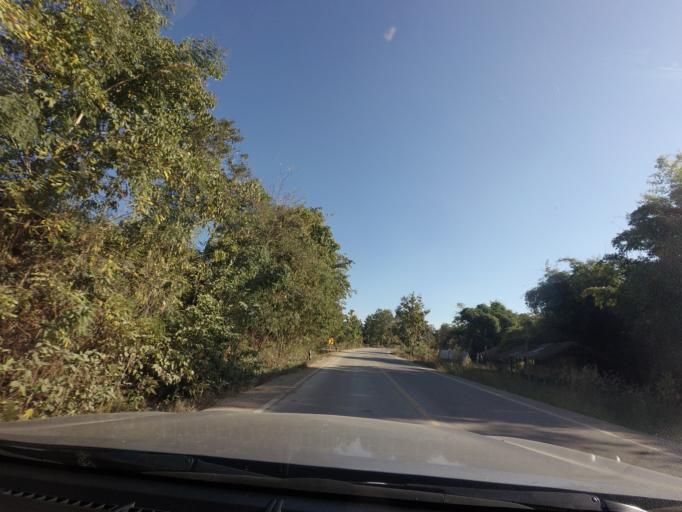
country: TH
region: Lampang
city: Chae Hom
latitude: 18.5361
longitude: 99.6424
